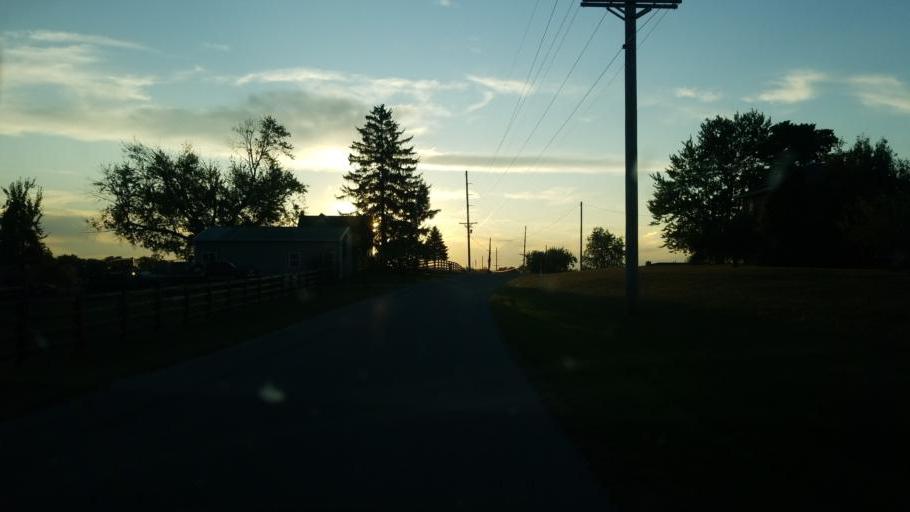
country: US
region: Ohio
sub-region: Delaware County
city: Ashley
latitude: 40.3603
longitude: -82.8834
